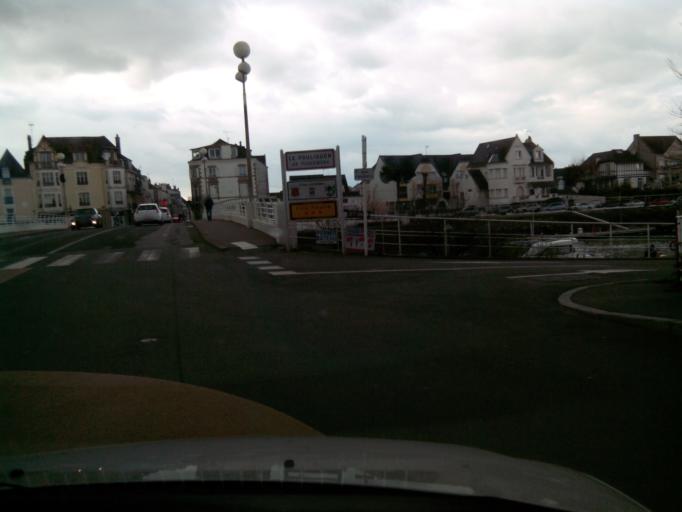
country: FR
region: Pays de la Loire
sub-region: Departement de la Loire-Atlantique
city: Le Pouliguen
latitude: 47.2783
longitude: -2.4270
